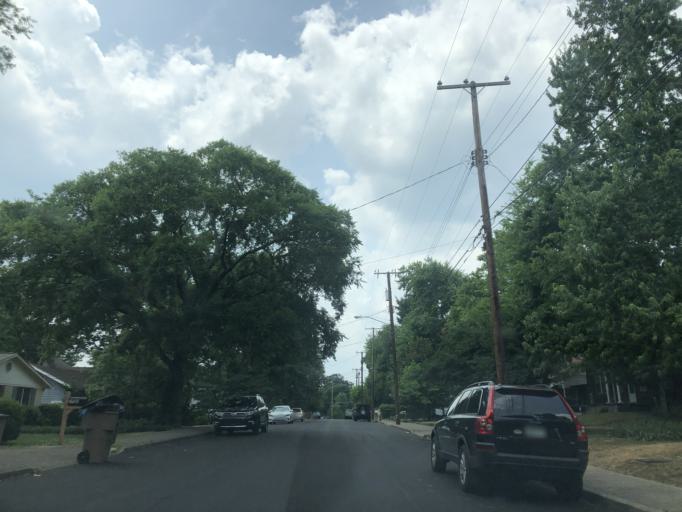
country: US
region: Tennessee
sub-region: Davidson County
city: Nashville
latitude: 36.1283
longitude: -86.8102
